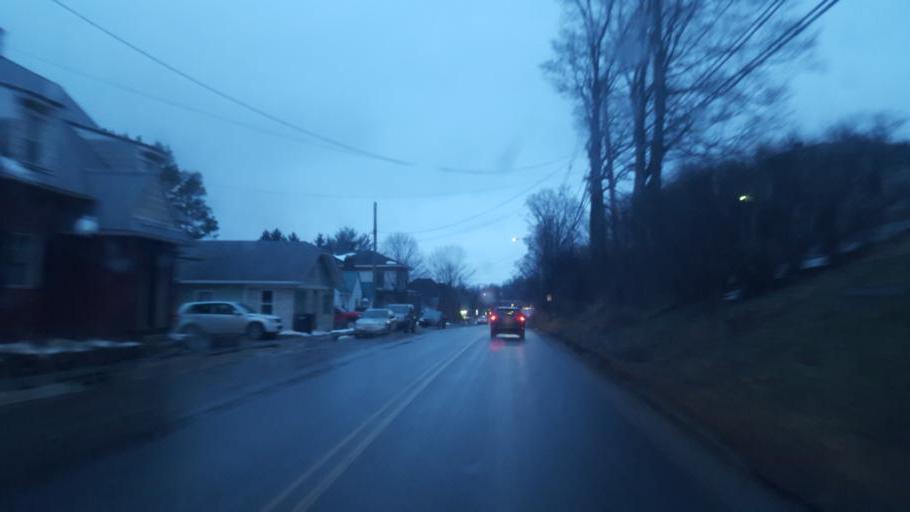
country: US
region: Pennsylvania
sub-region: McKean County
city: Port Allegany
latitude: 41.8070
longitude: -78.2783
